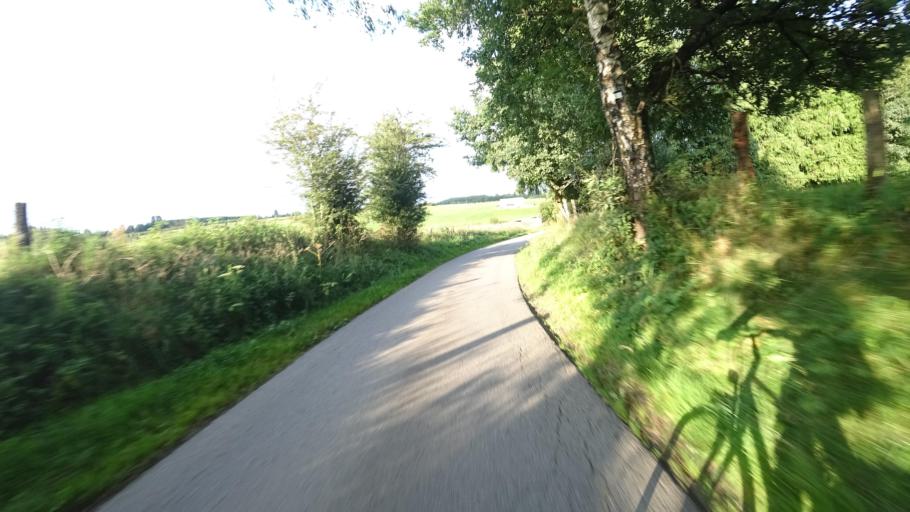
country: BE
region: Wallonia
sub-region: Province du Luxembourg
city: Neufchateau
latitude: 49.8545
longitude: 5.3582
